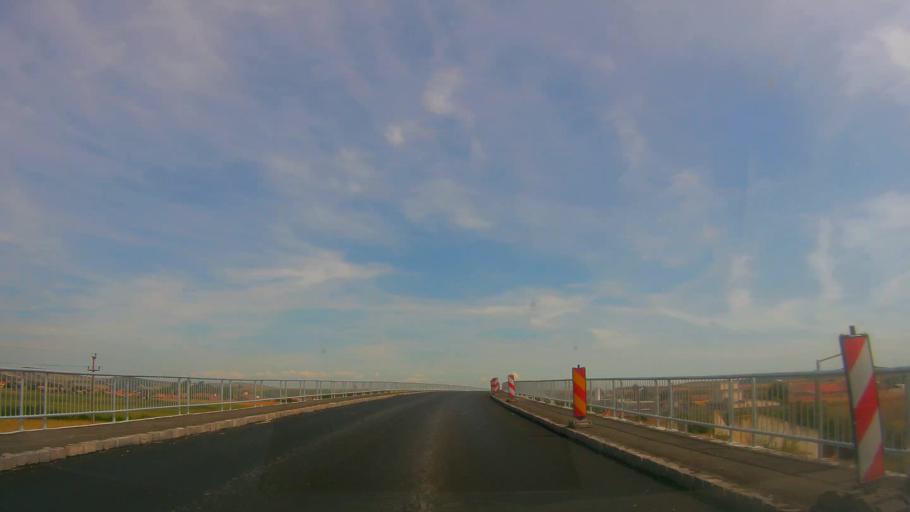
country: RO
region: Mures
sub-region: Comuna Sanpaul
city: Sanpaul
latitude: 46.4499
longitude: 24.3434
